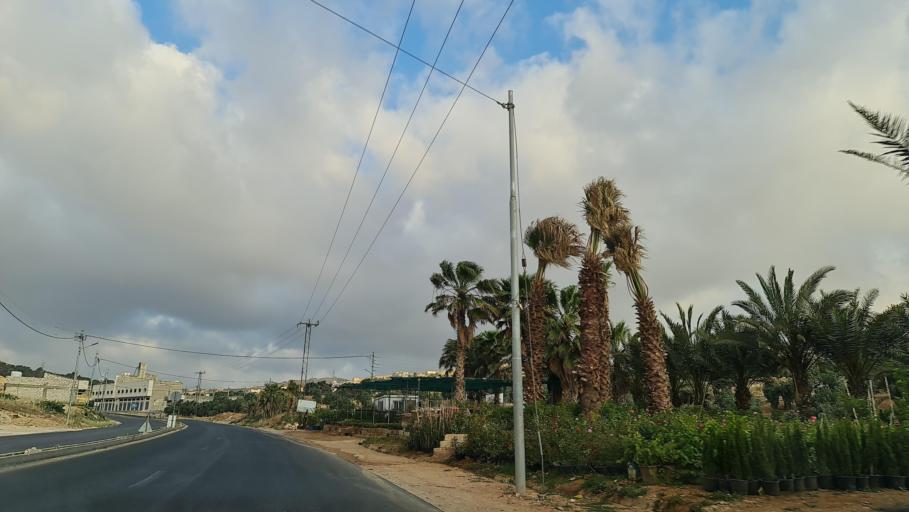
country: JO
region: Amman
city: Al Jubayhah
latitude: 32.0928
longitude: 35.9410
